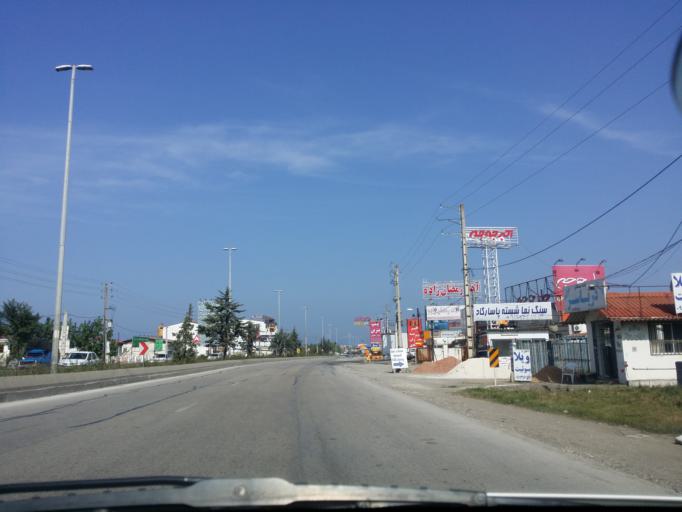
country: IR
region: Mazandaran
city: Chalus
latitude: 36.6765
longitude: 51.3967
